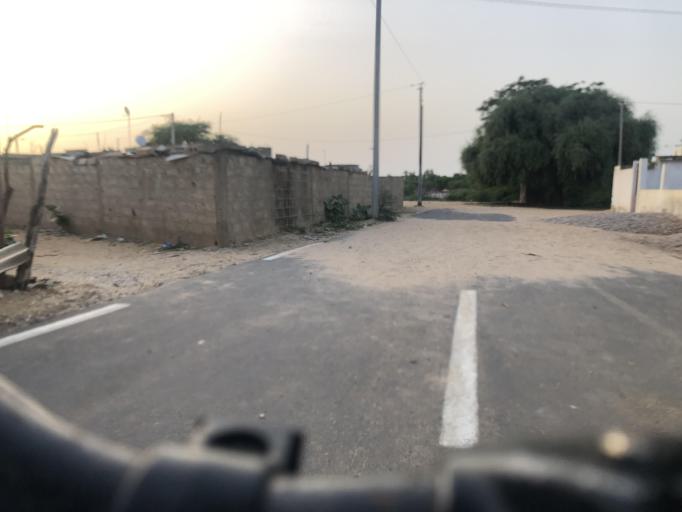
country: SN
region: Saint-Louis
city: Saint-Louis
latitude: 16.0697
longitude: -16.4279
